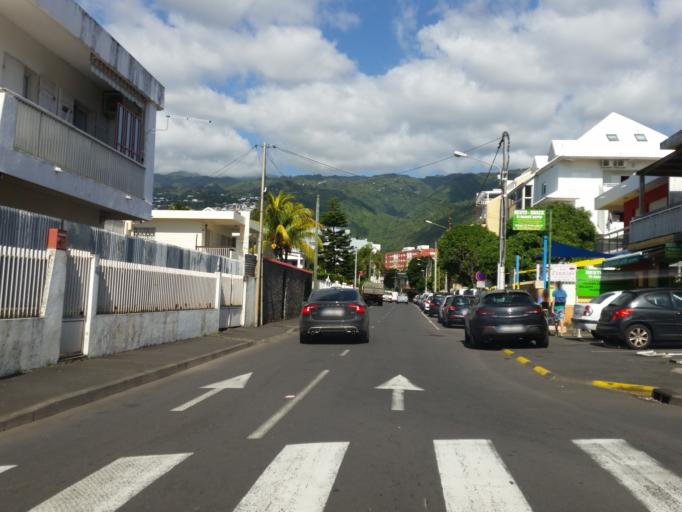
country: RE
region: Reunion
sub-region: Reunion
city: Saint-Denis
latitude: -20.8868
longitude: 55.4586
